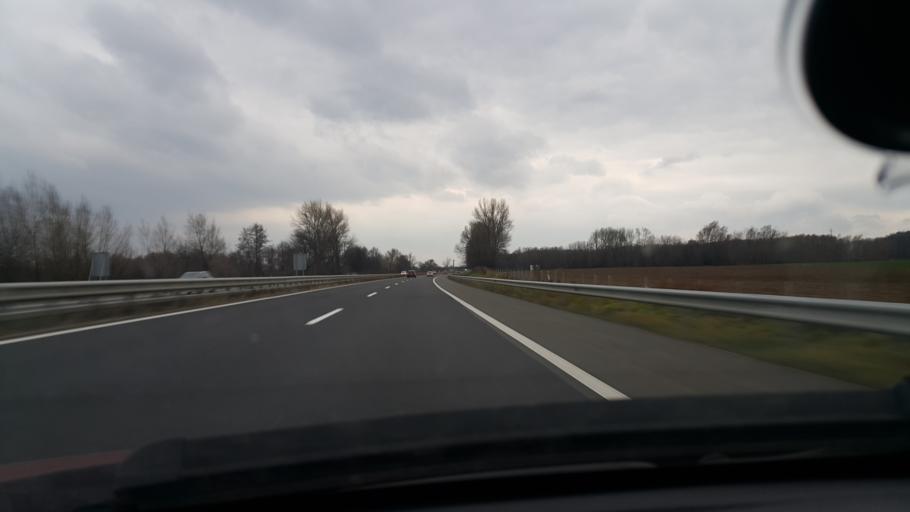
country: SI
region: Hoce-Slivnica
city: Hotinja Vas
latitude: 46.4598
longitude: 15.6559
